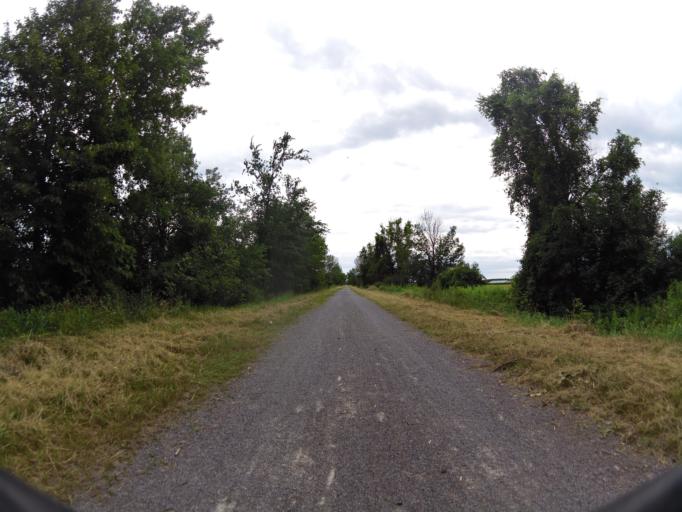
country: CA
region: Ontario
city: Ottawa
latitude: 45.1637
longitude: -75.6156
